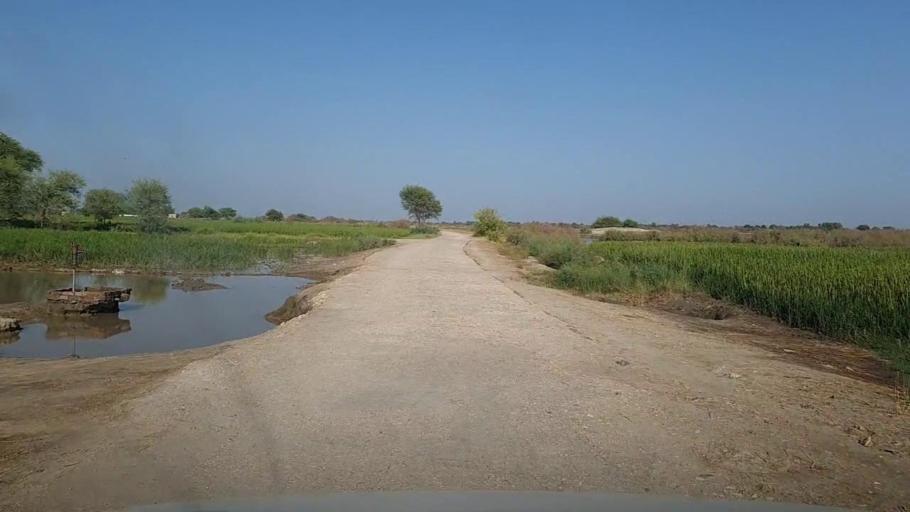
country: PK
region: Sindh
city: Kandhkot
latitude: 28.2793
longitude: 69.3201
